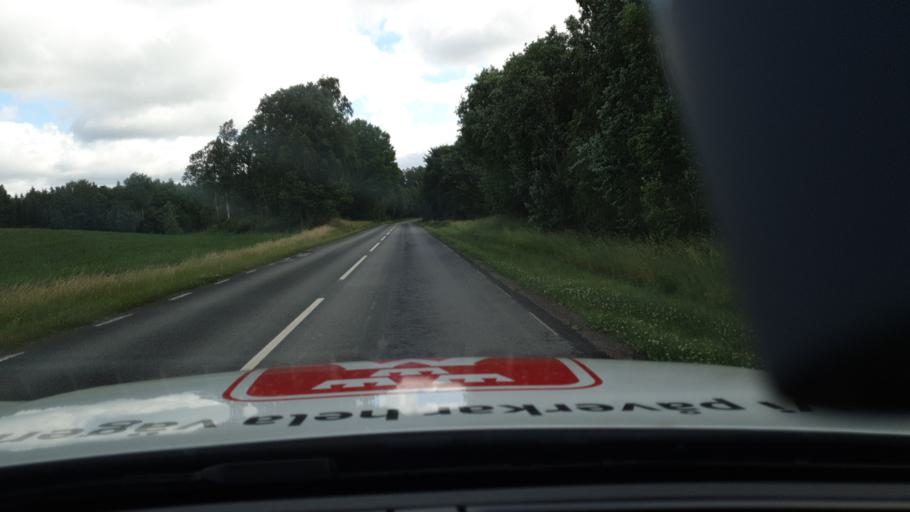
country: SE
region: Vaestra Goetaland
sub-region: Falkopings Kommun
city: Floby
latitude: 58.2323
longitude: 13.4176
